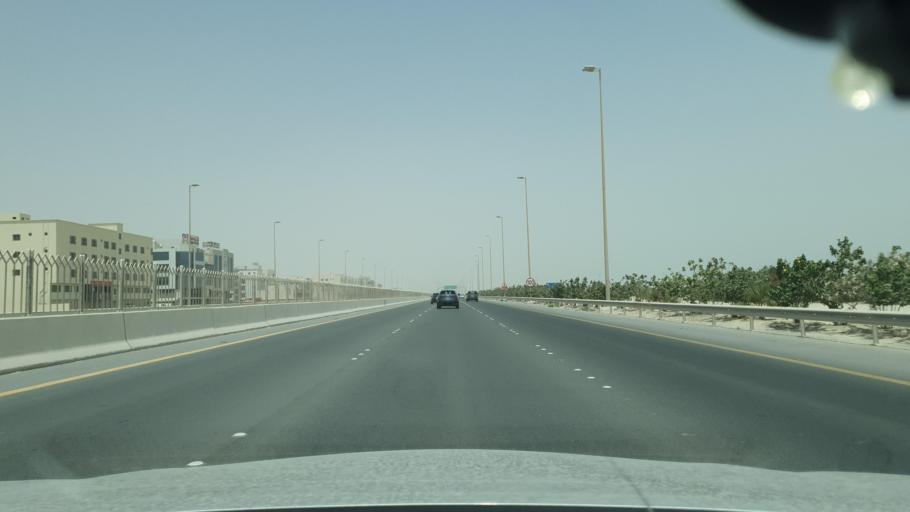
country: BH
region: Muharraq
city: Al Hadd
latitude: 26.2798
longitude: 50.6536
